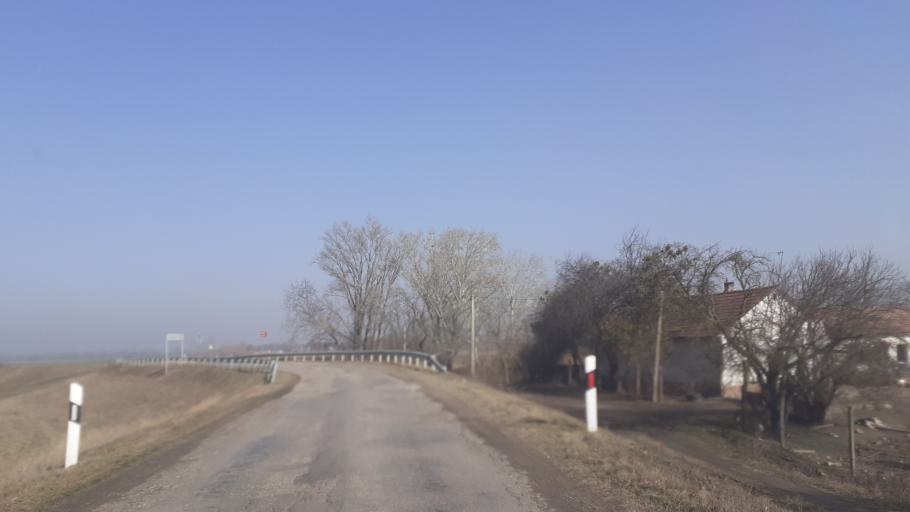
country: HU
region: Pest
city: Domsod
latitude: 47.0561
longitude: 18.9971
